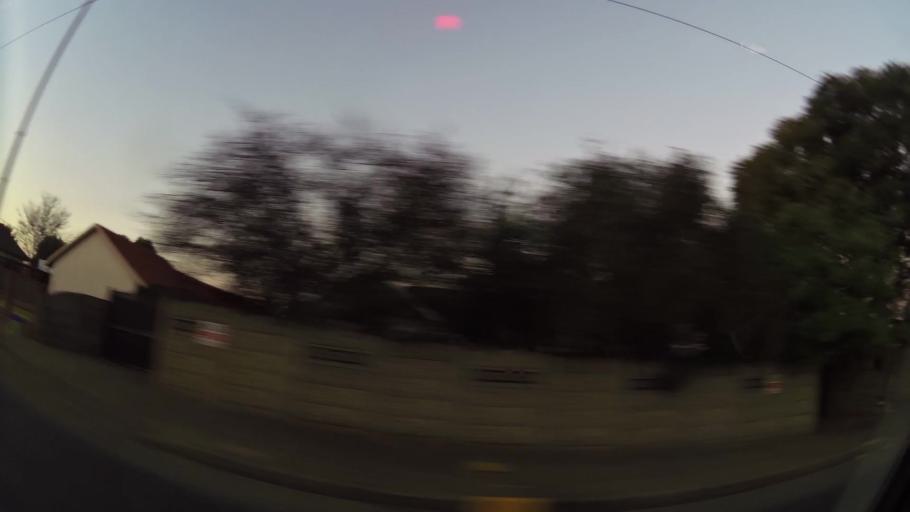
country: ZA
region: Gauteng
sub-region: Ekurhuleni Metropolitan Municipality
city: Germiston
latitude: -26.2609
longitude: 28.1621
